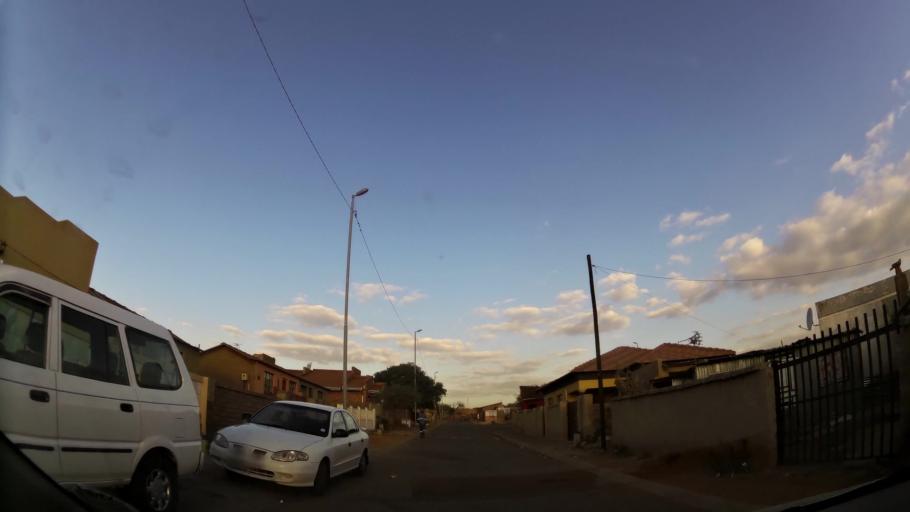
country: ZA
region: Gauteng
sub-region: West Rand District Municipality
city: Krugersdorp
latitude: -26.0778
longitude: 27.7540
